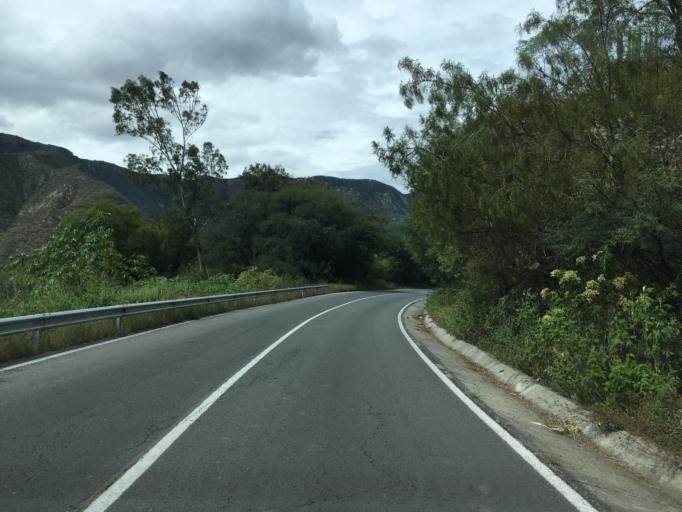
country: MX
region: Hidalgo
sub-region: San Agustin Metzquititlan
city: Mezquititlan
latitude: 20.5177
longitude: -98.7145
